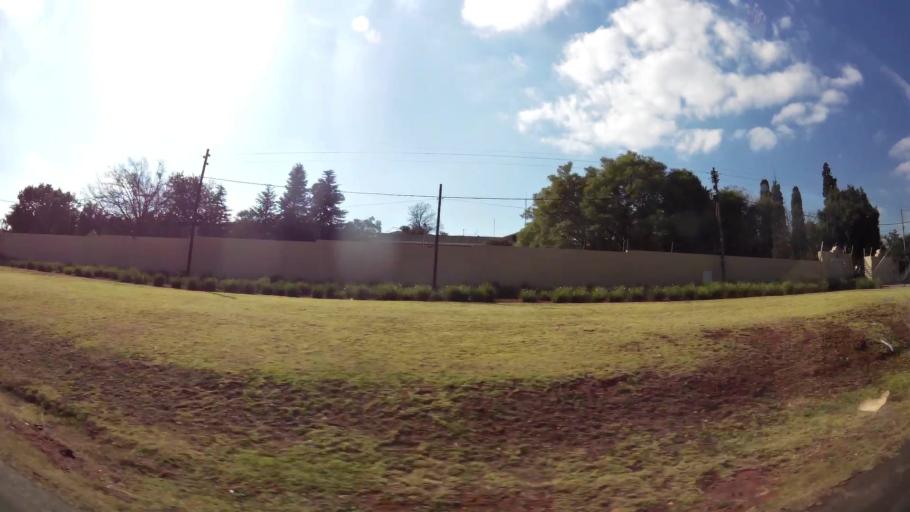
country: ZA
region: Gauteng
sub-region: West Rand District Municipality
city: Krugersdorp
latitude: -26.0449
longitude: 27.7495
